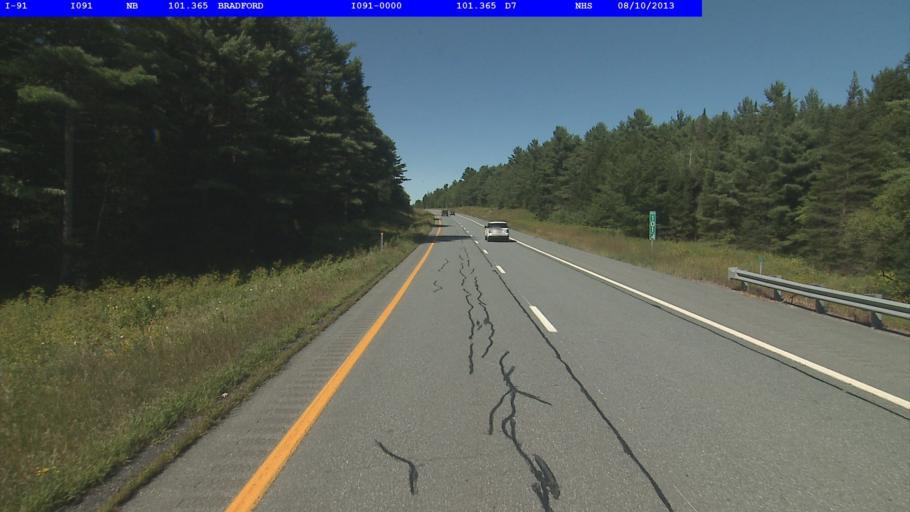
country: US
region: New Hampshire
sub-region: Grafton County
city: Haverhill
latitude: 44.0335
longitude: -72.1111
